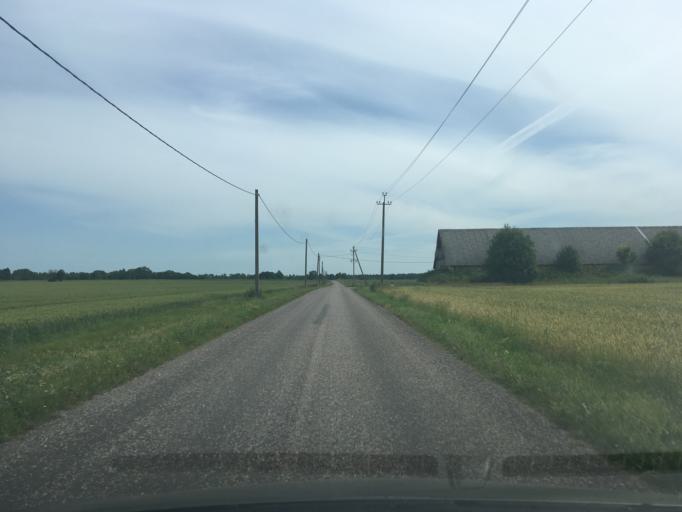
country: EE
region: Raplamaa
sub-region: Rapla vald
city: Rapla
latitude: 59.0277
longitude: 24.7913
